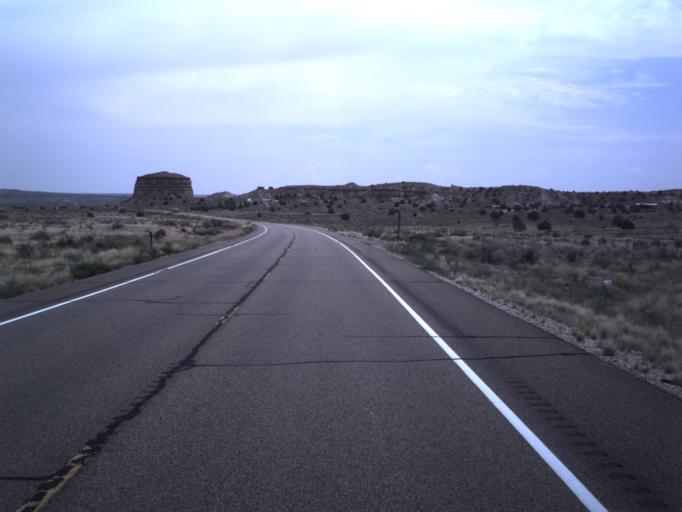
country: US
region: Arizona
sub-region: Coconino County
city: Page
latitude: 37.1133
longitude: -111.9328
